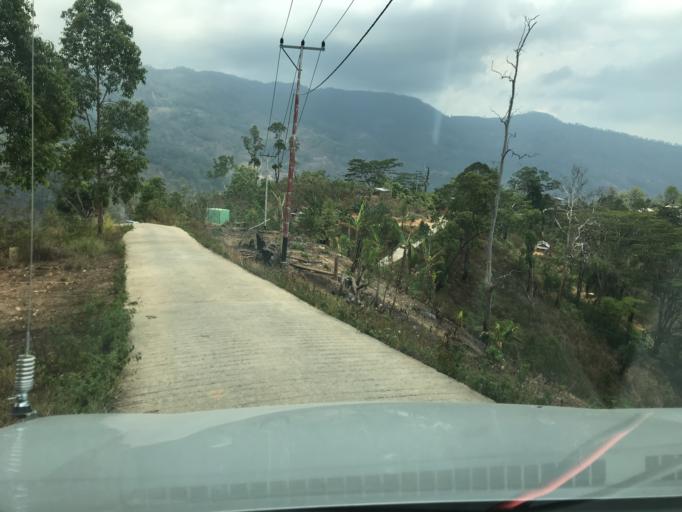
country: TL
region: Dili
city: Dili
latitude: -8.6131
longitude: 125.5711
